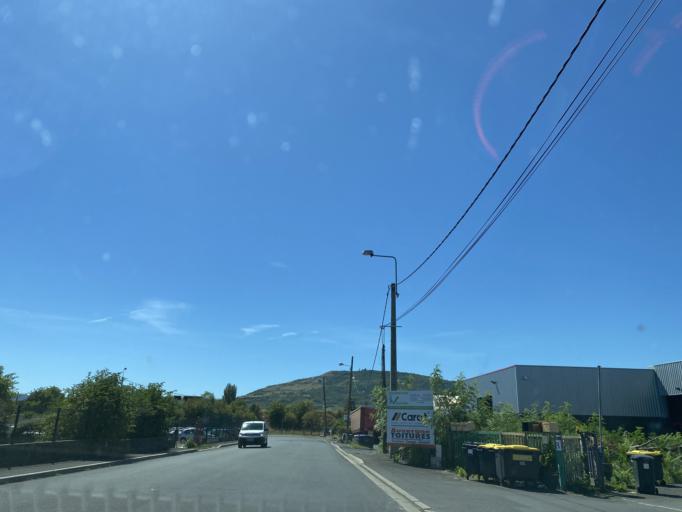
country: FR
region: Auvergne
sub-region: Departement du Puy-de-Dome
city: Perignat-les-Sarlieve
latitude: 45.7419
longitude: 3.1647
